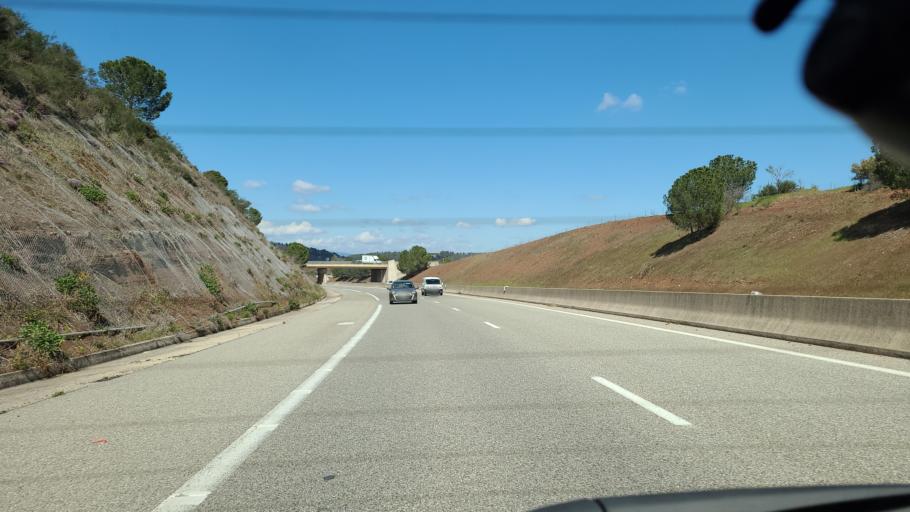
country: FR
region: Provence-Alpes-Cote d'Azur
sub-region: Departement du Var
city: Le Cannet-des-Maures
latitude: 43.3846
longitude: 6.3589
